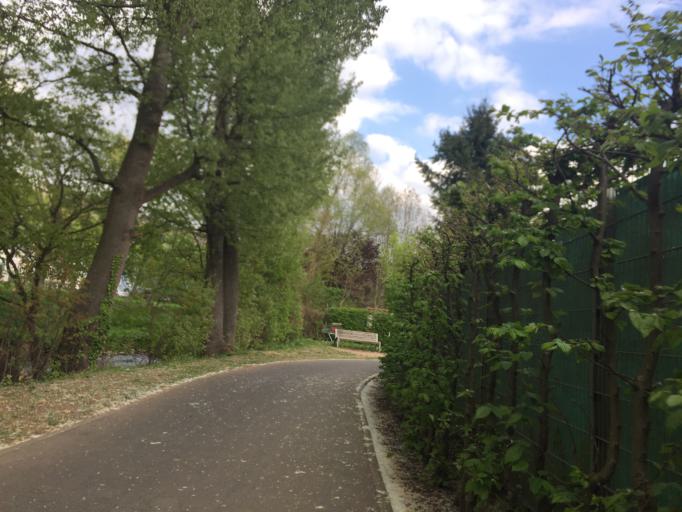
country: DE
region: Bavaria
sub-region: Regierungsbezirk Unterfranken
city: Glattbach
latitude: 49.9880
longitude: 9.1450
